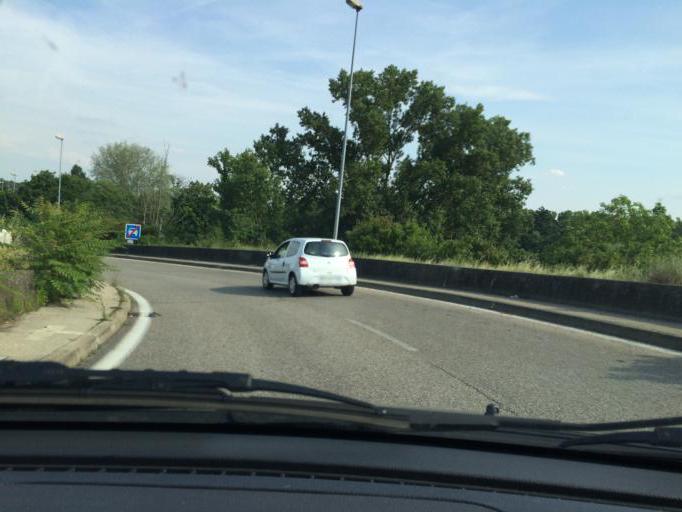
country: FR
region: Rhone-Alpes
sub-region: Departement du Rhone
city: Villeurbanne
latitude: 45.7900
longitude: 4.8839
